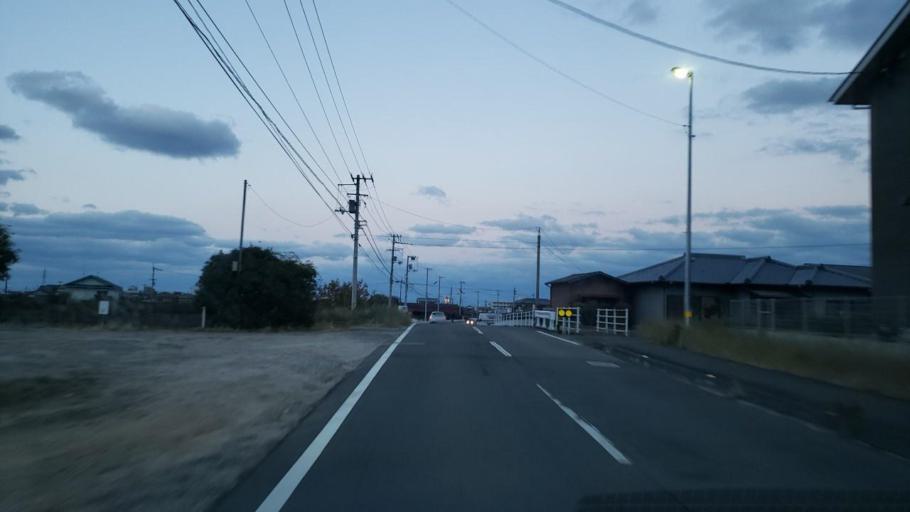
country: JP
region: Tokushima
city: Kamojimacho-jogejima
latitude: 34.2344
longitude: 134.3469
